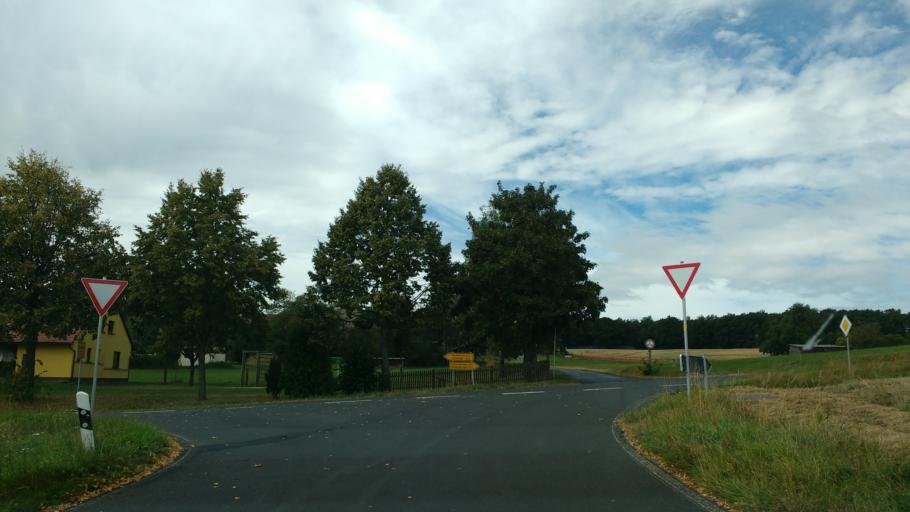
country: DE
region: Bavaria
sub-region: Regierungsbezirk Unterfranken
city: Geiselwind
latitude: 49.7956
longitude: 10.5135
